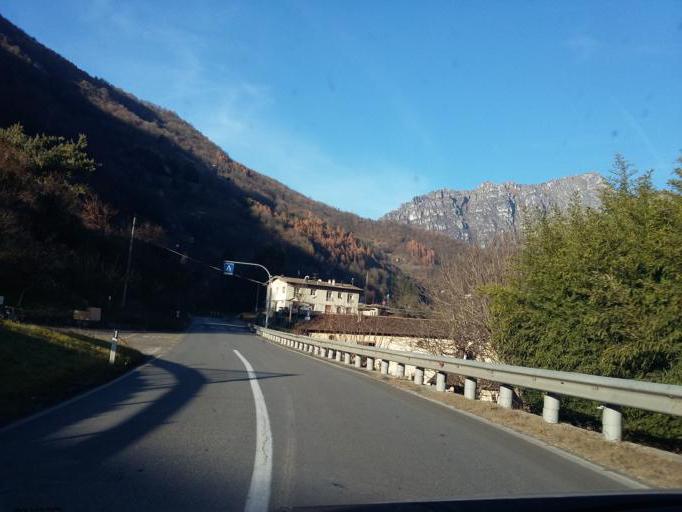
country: IT
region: Lombardy
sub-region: Provincia di Brescia
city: Lavenone
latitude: 45.7306
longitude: 10.4346
